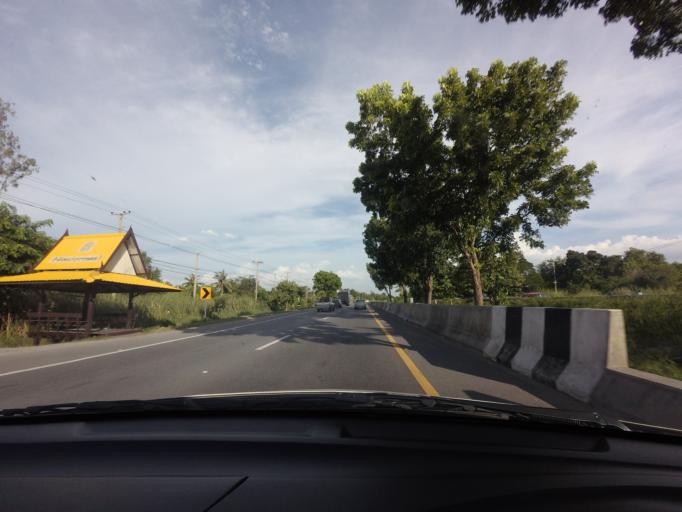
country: TH
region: Pathum Thani
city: Lat Lum Kaeo
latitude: 14.0021
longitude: 100.3726
